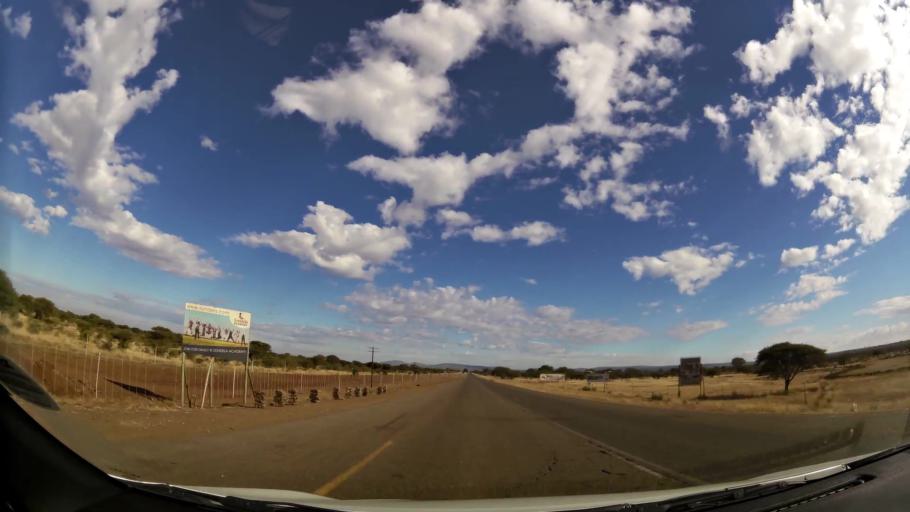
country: ZA
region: Limpopo
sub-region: Waterberg District Municipality
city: Bela-Bela
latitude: -24.9176
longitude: 28.3694
